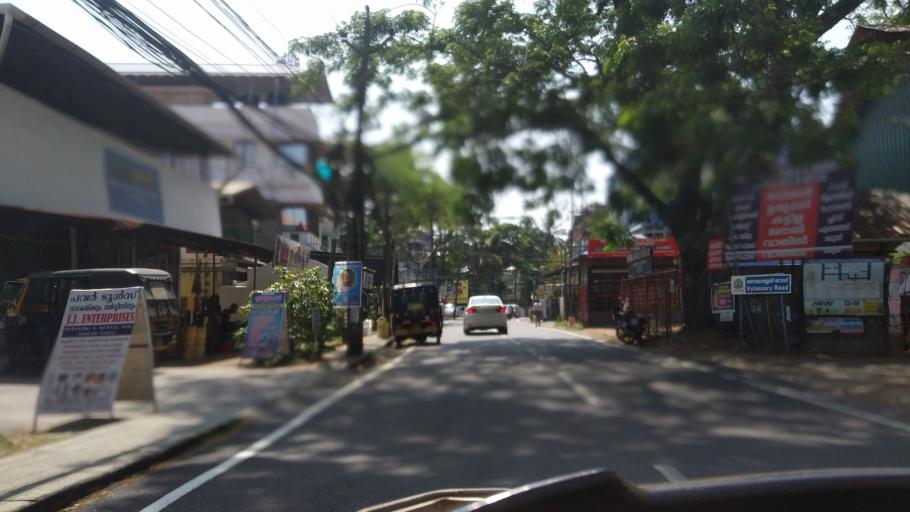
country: IN
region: Kerala
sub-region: Ernakulam
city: Cochin
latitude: 9.9950
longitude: 76.3083
